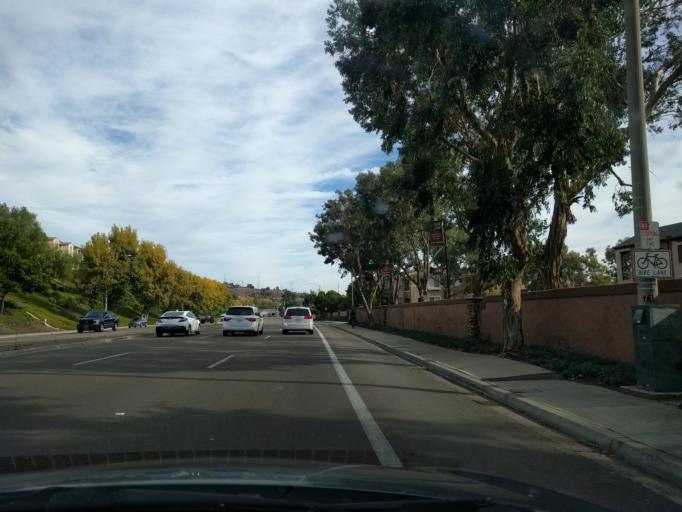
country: US
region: California
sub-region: San Diego County
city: San Diego
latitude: 32.7793
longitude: -117.1339
